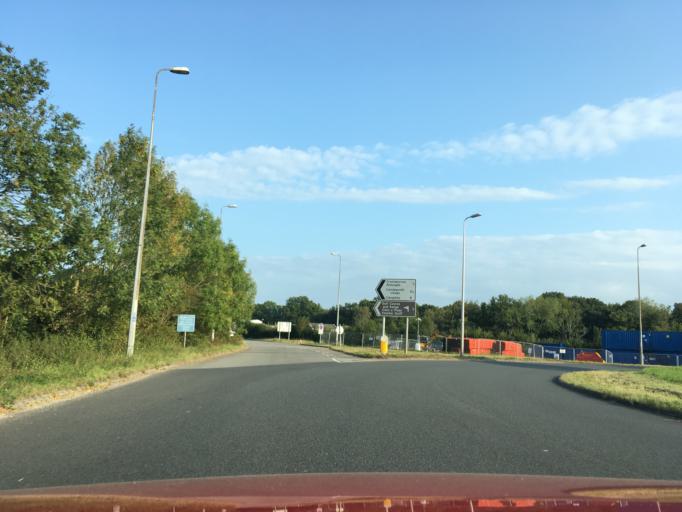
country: GB
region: Wales
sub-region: Torfaen County Borough
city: Cwmbran
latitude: 51.6681
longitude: -3.0052
